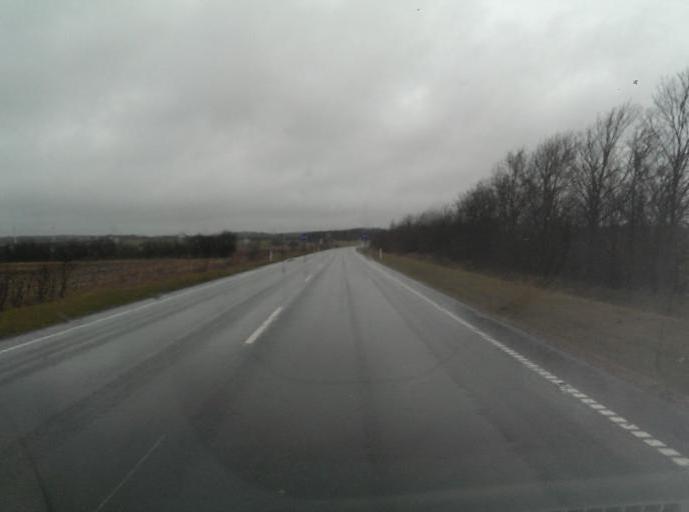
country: DK
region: South Denmark
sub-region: Varde Kommune
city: Varde
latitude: 55.6669
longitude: 8.4967
